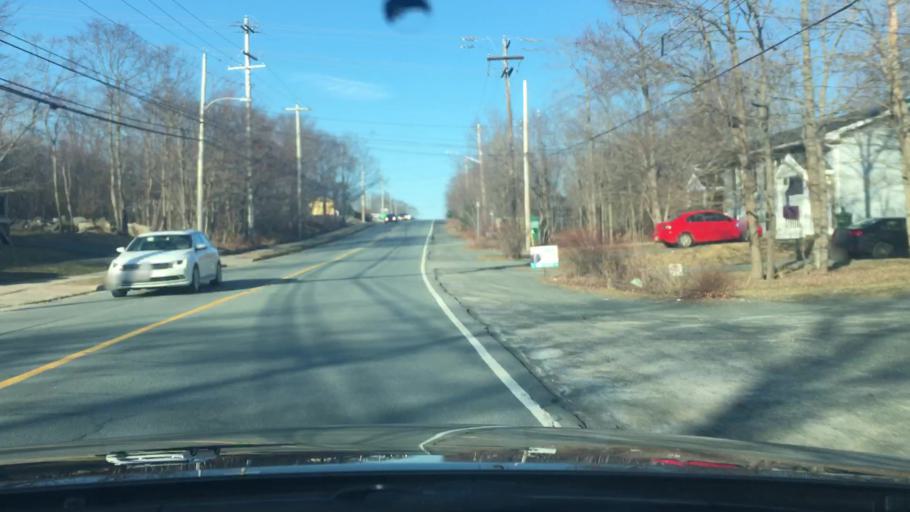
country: CA
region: Nova Scotia
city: Dartmouth
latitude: 44.7406
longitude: -63.6431
